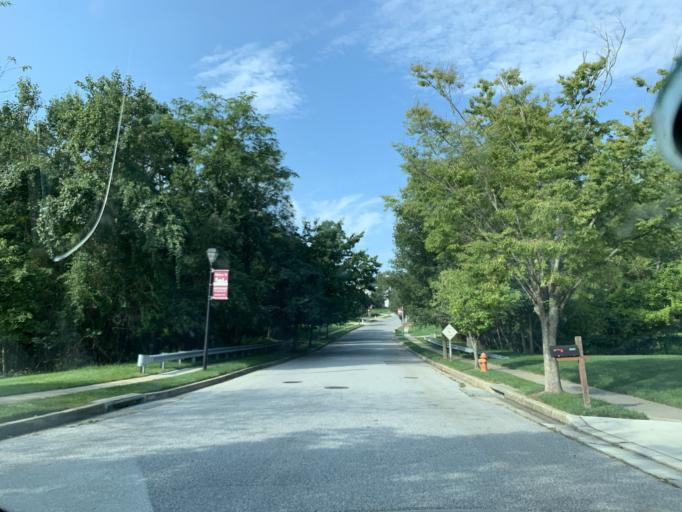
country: US
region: Maryland
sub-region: Baltimore County
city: Randallstown
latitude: 39.3904
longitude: -76.7958
